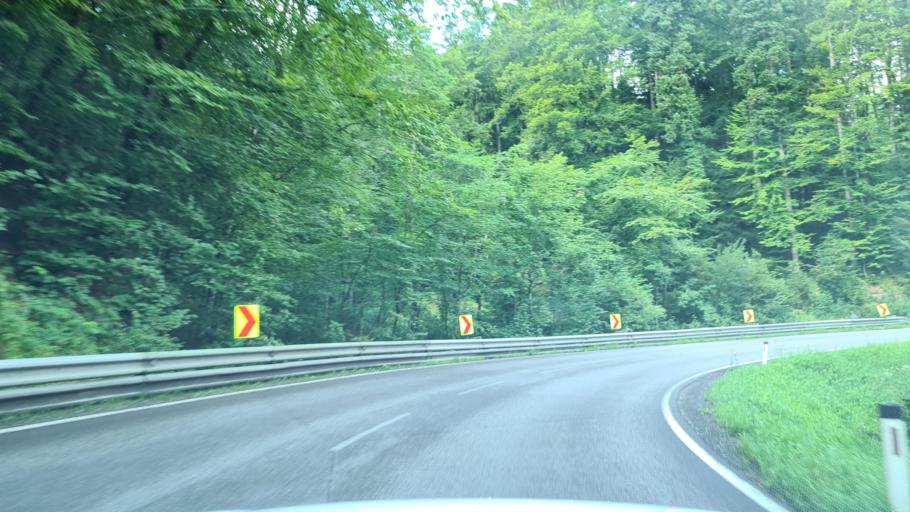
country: AT
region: Vorarlberg
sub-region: Politischer Bezirk Bregenz
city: Egg
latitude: 47.4533
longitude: 9.8709
